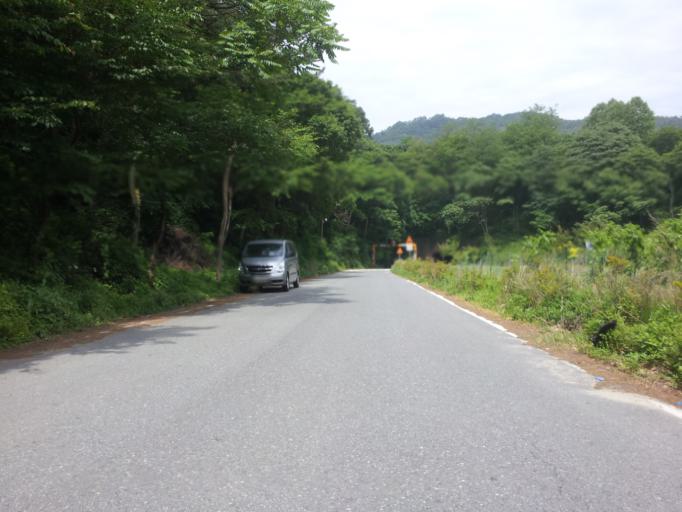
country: KR
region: Daejeon
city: Daejeon
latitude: 36.3350
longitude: 127.4908
